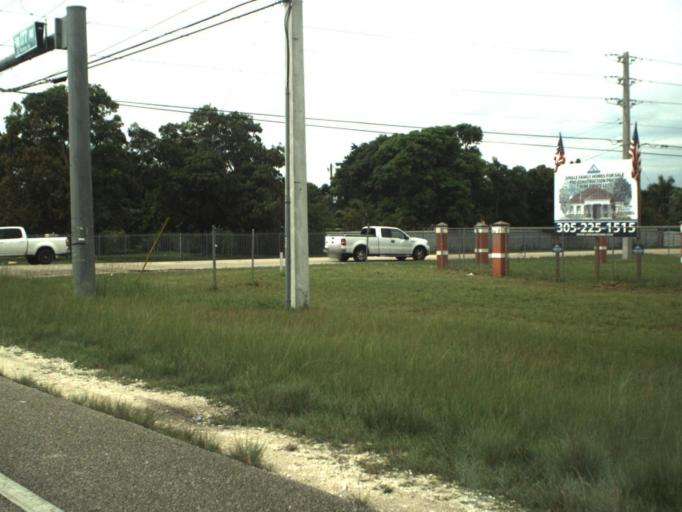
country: US
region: Florida
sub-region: Miami-Dade County
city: Richmond West
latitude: 25.5655
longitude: -80.4783
